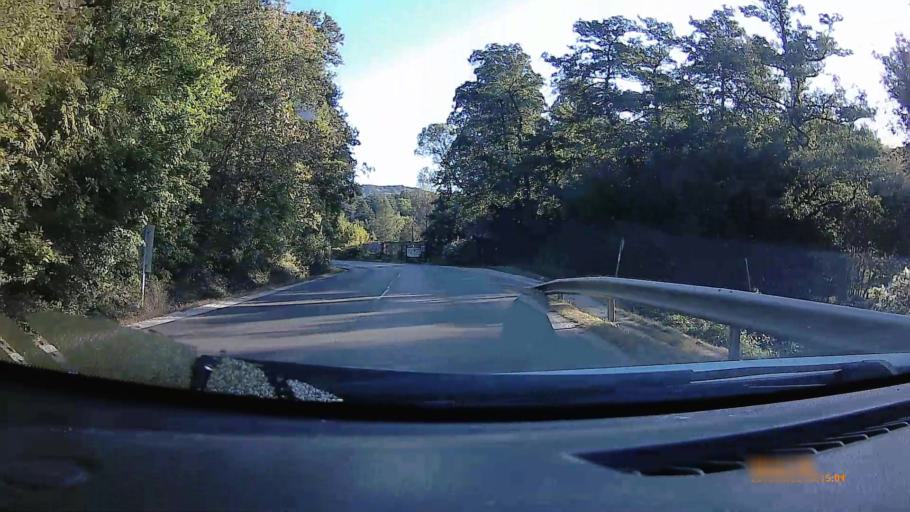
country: HU
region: Borsod-Abauj-Zemplen
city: Sajobabony
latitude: 48.1145
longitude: 20.6534
